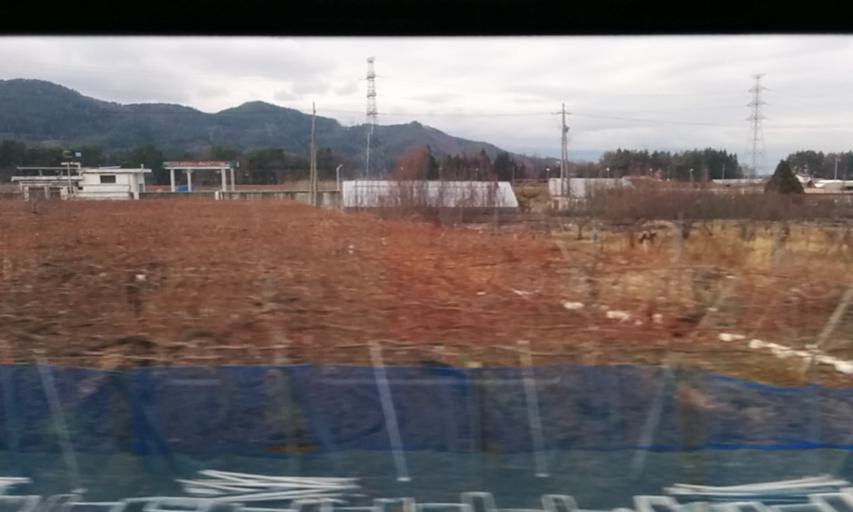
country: JP
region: Nagano
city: Shiojiri
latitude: 36.0948
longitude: 137.9253
